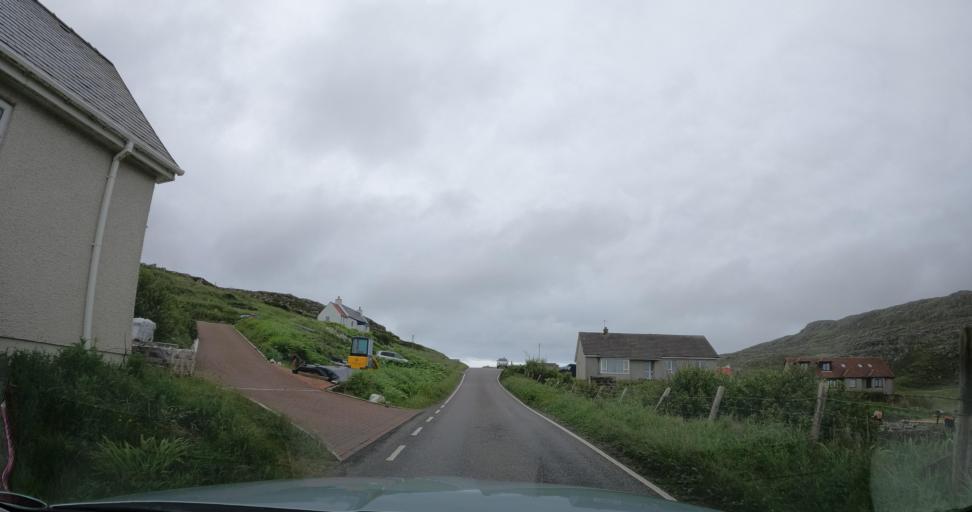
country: GB
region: Scotland
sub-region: Eilean Siar
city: Barra
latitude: 56.9601
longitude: -7.5055
